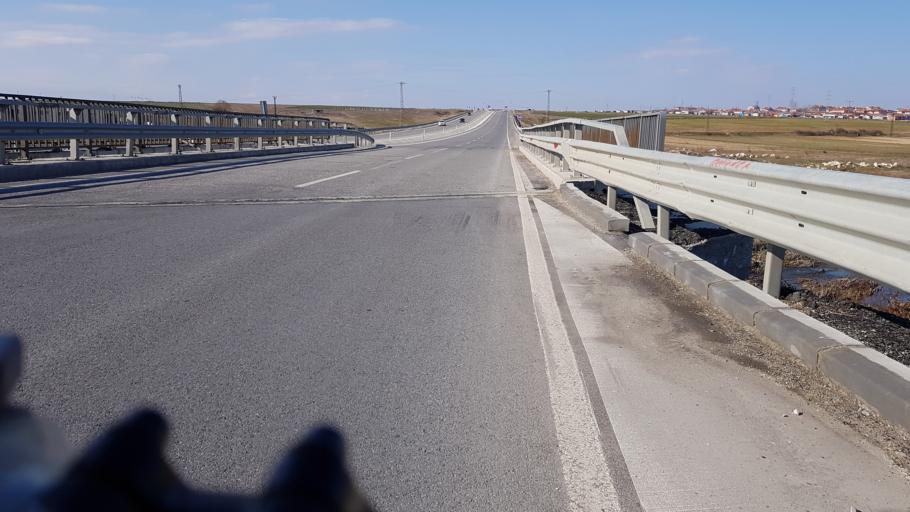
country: TR
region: Tekirdag
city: Saray
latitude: 41.4251
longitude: 27.9128
